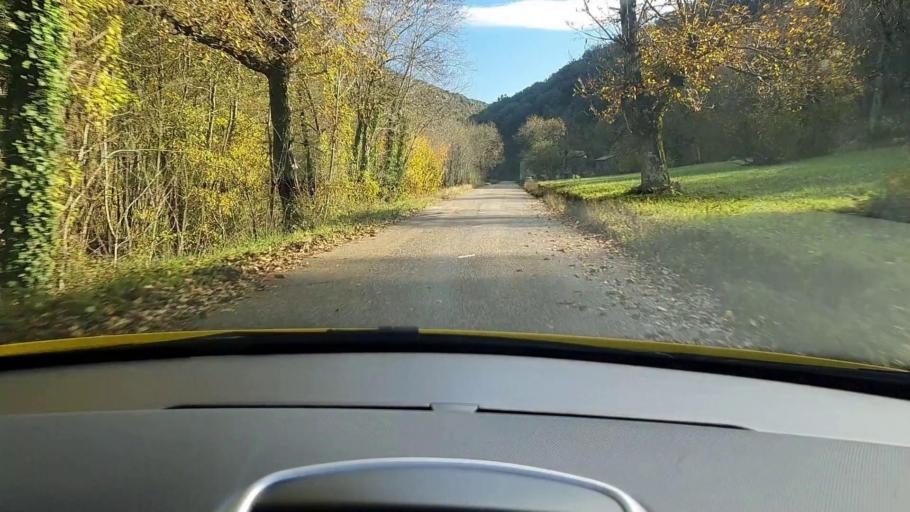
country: FR
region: Languedoc-Roussillon
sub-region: Departement du Gard
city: Valleraugue
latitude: 44.1689
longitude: 3.6533
